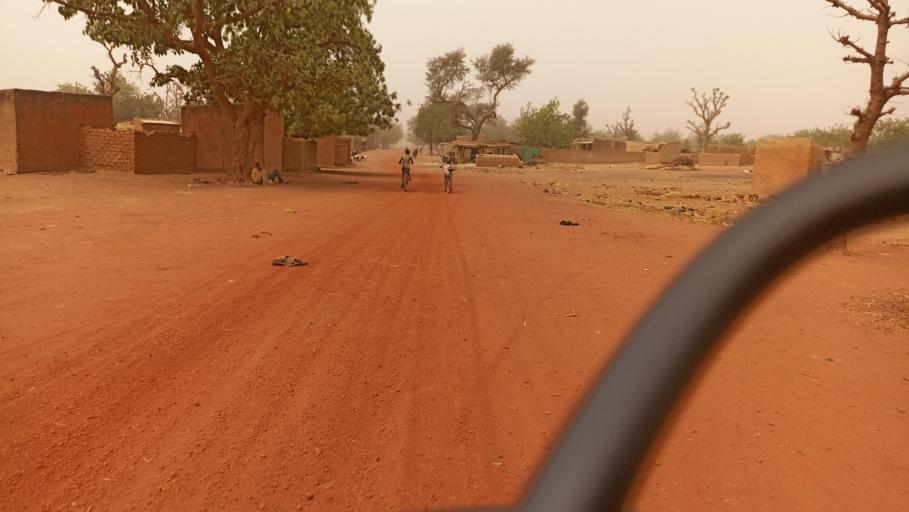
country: BF
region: Nord
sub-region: Province du Zondoma
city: Gourcy
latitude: 13.2645
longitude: -2.5440
